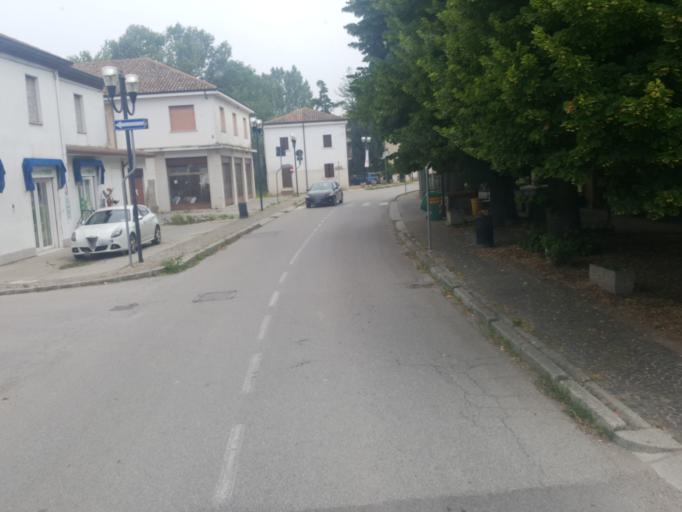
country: IT
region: Veneto
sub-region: Provincia di Rovigo
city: Canaro
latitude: 44.9342
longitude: 11.6760
